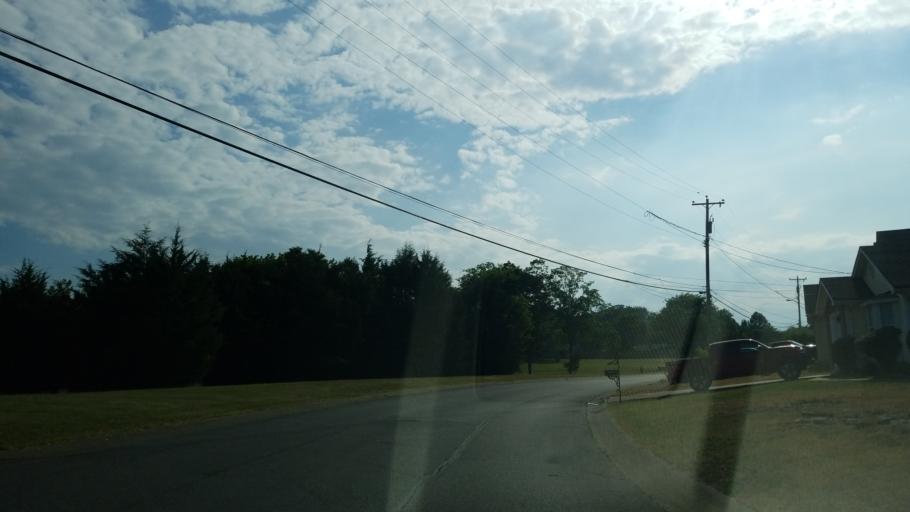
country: US
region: Tennessee
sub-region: Rutherford County
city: La Vergne
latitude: 36.0382
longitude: -86.5836
